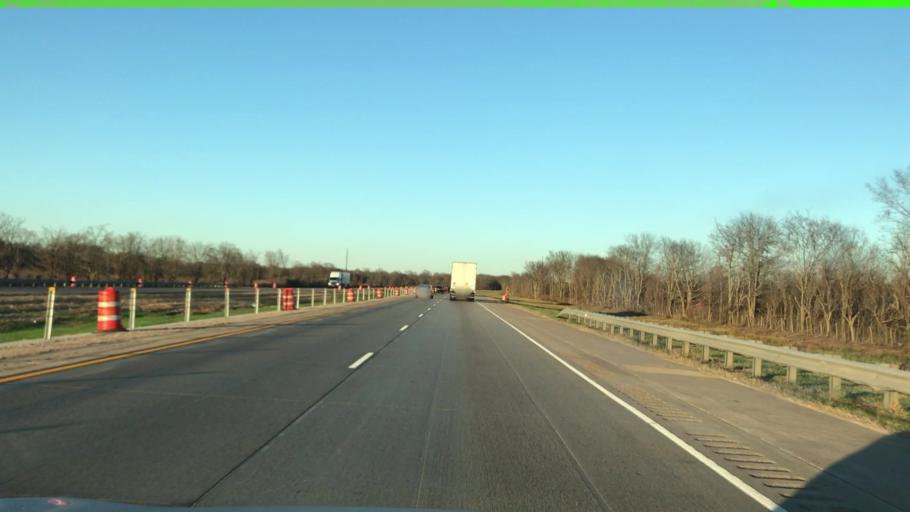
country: US
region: Arkansas
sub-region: Miller County
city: Texarkana
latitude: 33.5782
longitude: -93.8446
